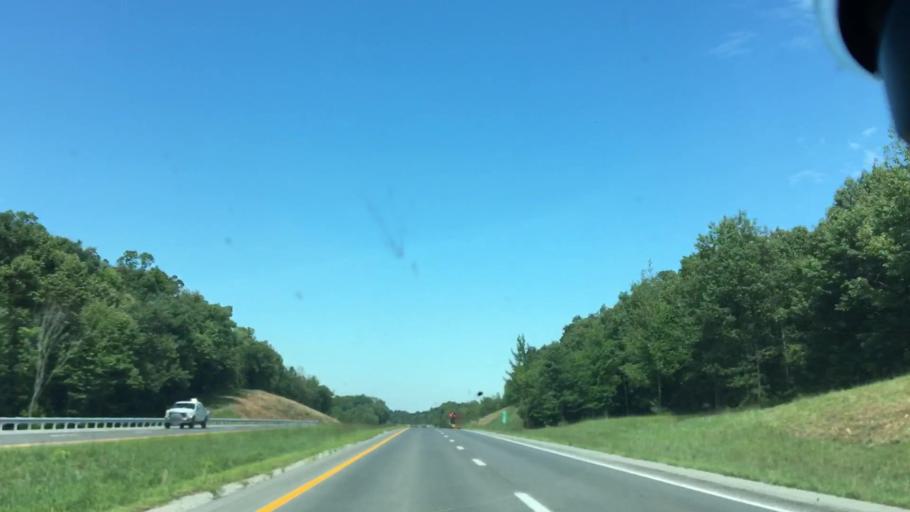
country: US
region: Kentucky
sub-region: Webster County
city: Sebree
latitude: 37.5193
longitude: -87.4750
